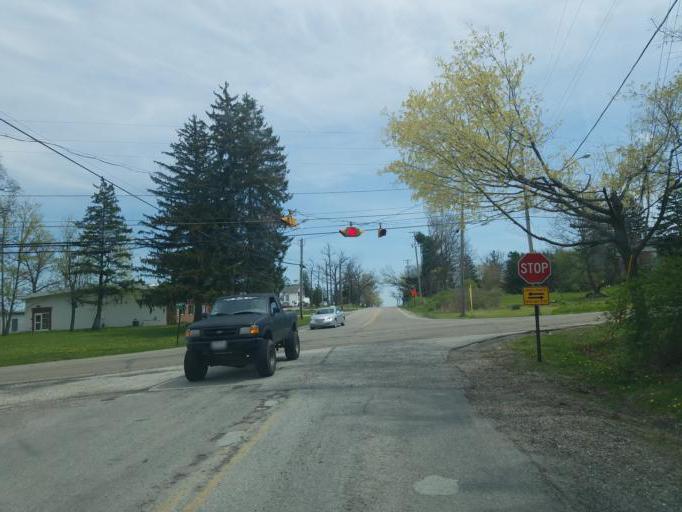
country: US
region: Ohio
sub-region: Summit County
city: Boston Heights
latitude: 41.2549
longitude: -81.5083
